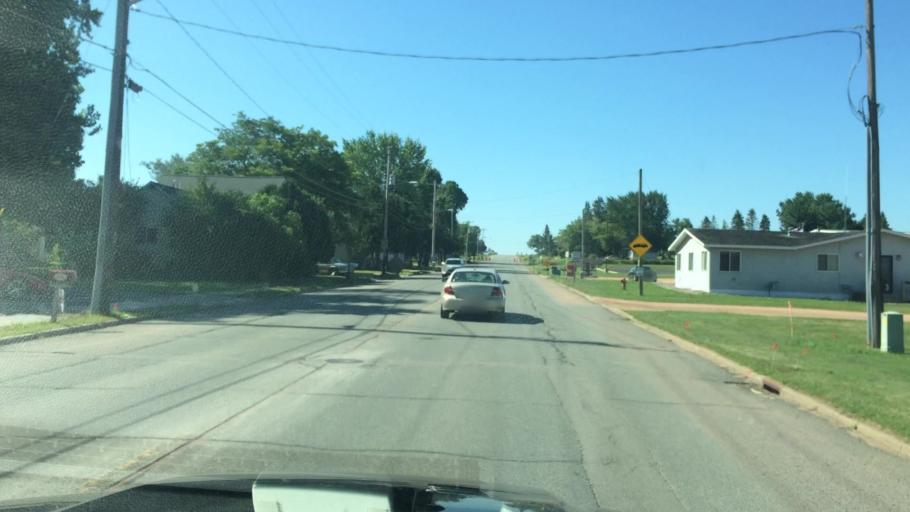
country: US
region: Wisconsin
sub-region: Marathon County
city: Stratford
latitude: 44.7966
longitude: -90.0792
